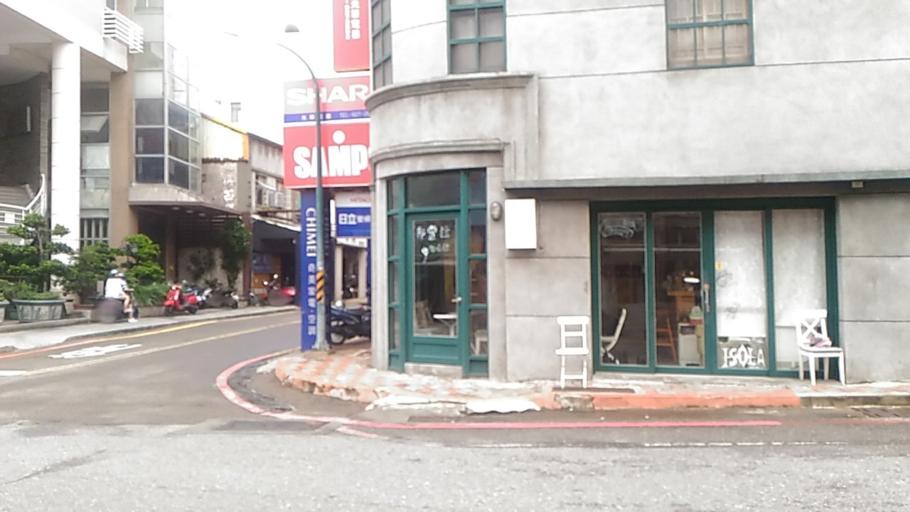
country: TW
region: Taiwan
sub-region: Penghu
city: Ma-kung
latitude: 23.5665
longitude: 119.5685
